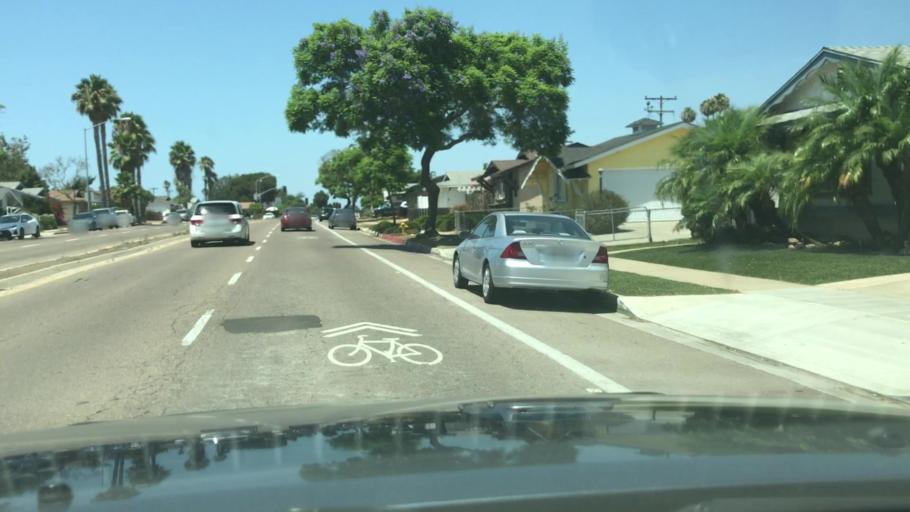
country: US
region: California
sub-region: San Diego County
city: La Jolla
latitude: 32.8358
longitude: -117.1949
